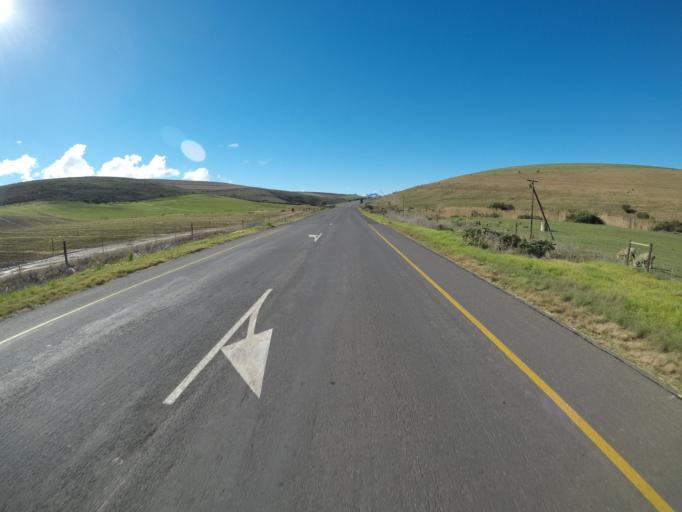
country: ZA
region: Western Cape
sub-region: Overberg District Municipality
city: Caledon
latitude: -34.1561
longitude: 19.4570
